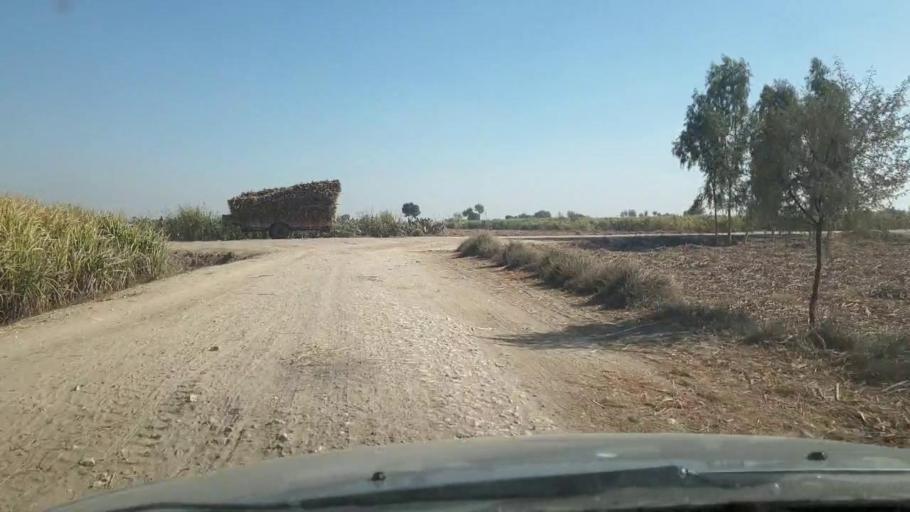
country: PK
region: Sindh
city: Ghotki
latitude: 28.0268
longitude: 69.2187
